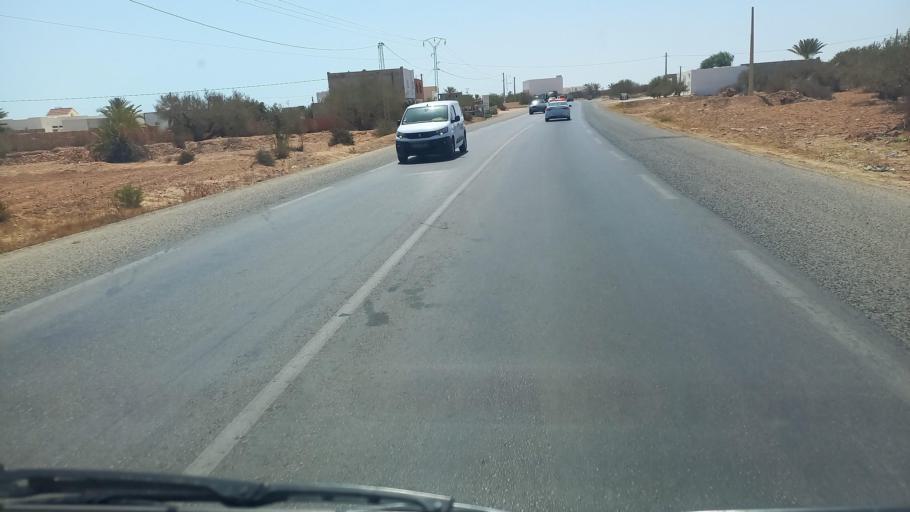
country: TN
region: Madanin
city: Houmt Souk
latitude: 33.8202
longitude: 10.8713
